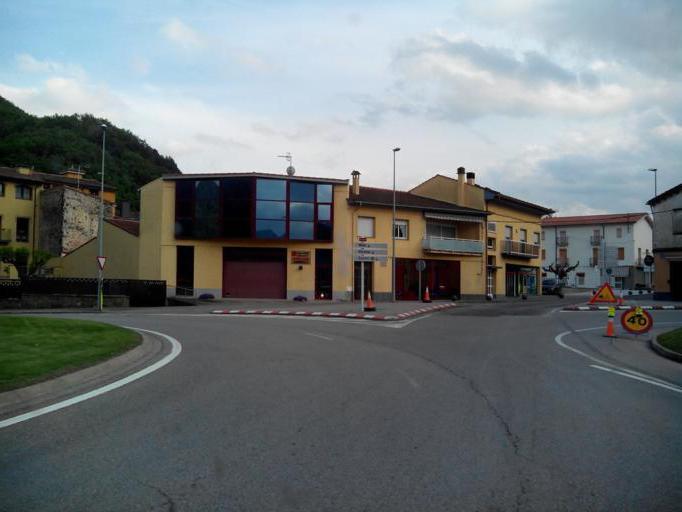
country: ES
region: Catalonia
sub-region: Provincia de Girona
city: Sant Joan les Fonts
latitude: 42.2079
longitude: 2.4976
